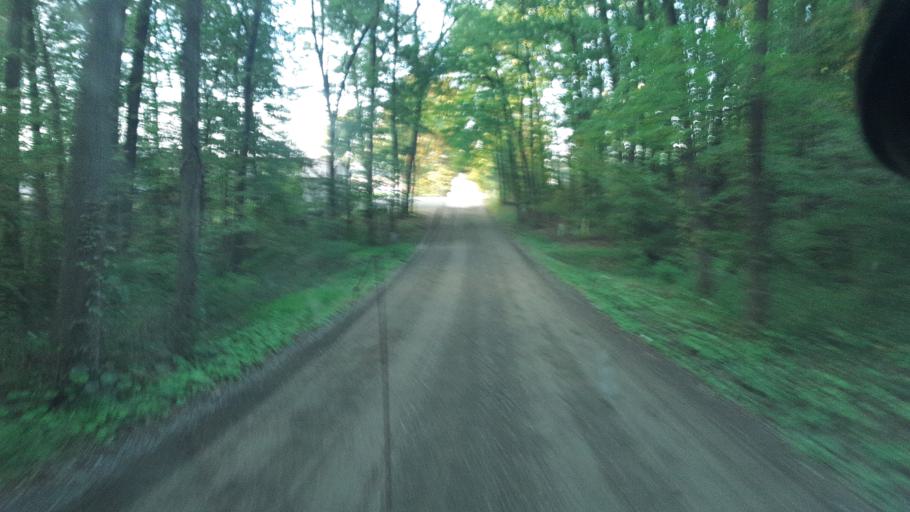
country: US
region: Ohio
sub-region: Tuscarawas County
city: Sugarcreek
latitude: 40.4585
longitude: -81.7279
